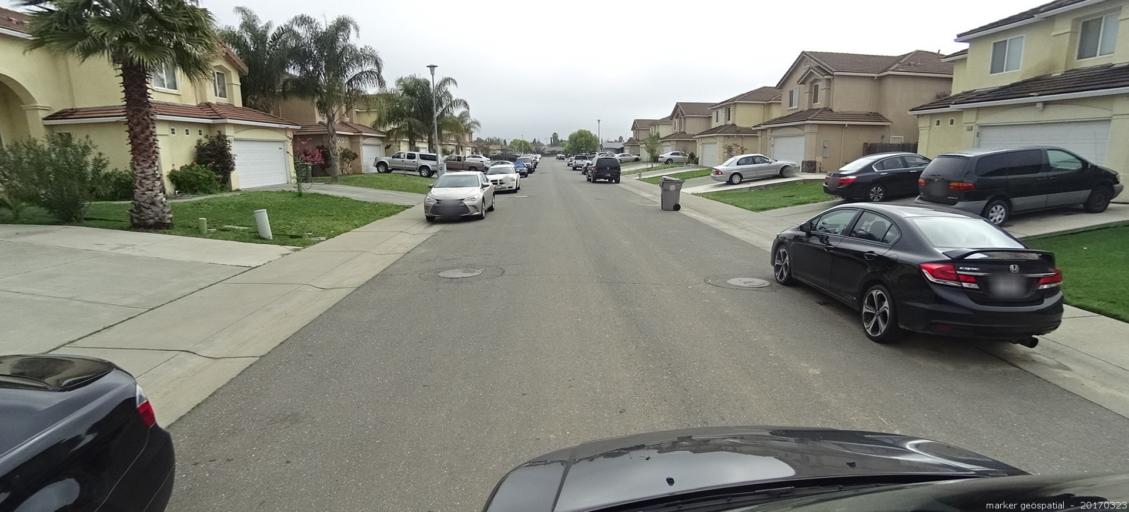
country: US
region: California
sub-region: Sacramento County
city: Florin
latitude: 38.5138
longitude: -121.4219
